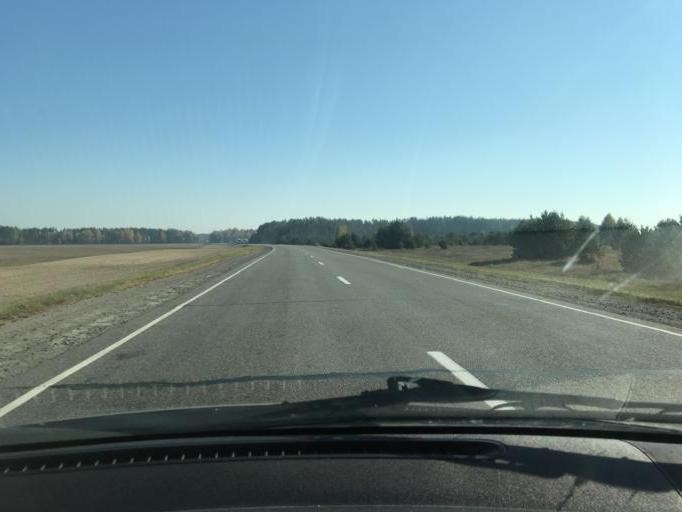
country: BY
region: Brest
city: Davyd-Haradok
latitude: 52.2492
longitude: 27.0707
